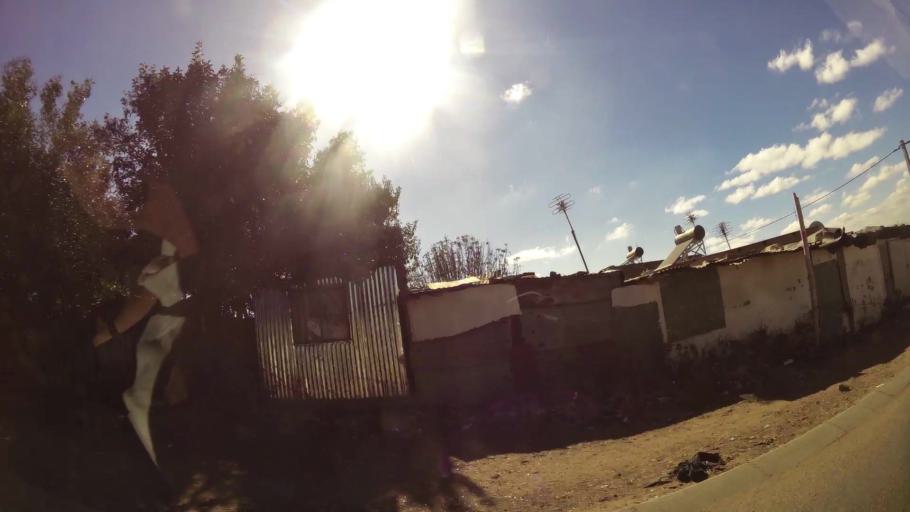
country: ZA
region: Gauteng
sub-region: Ekurhuleni Metropolitan Municipality
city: Tembisa
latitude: -26.0330
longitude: 28.1842
